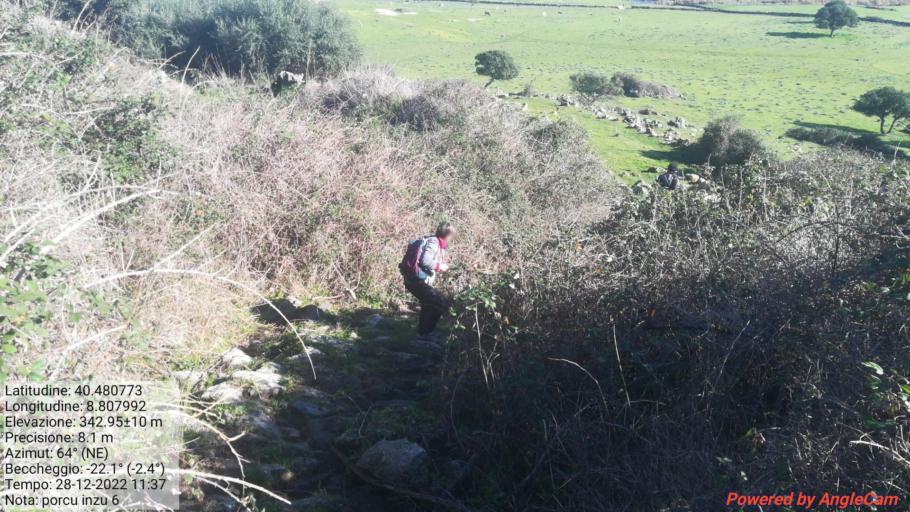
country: IT
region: Sardinia
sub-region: Provincia di Sassari
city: Torralba
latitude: 40.4808
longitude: 8.8080
